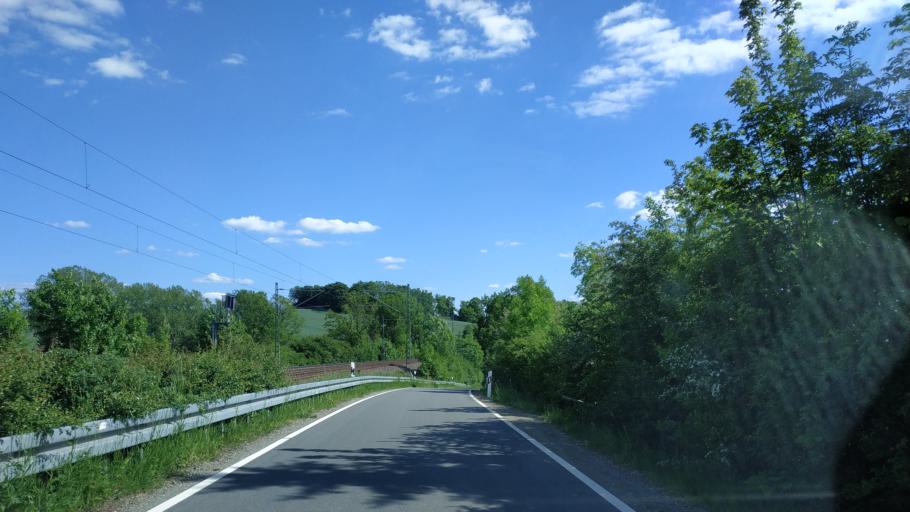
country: DE
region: Saxony
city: Pohl
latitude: 50.5636
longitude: 12.1718
